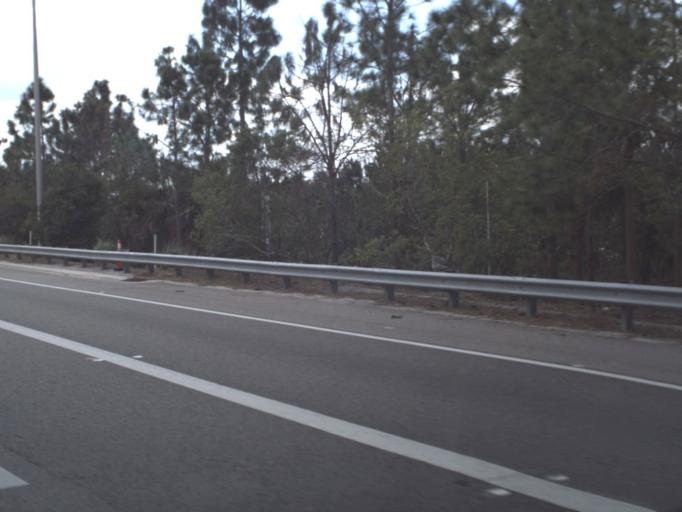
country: US
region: Florida
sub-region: Orange County
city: Ocoee
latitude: 28.5539
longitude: -81.5594
